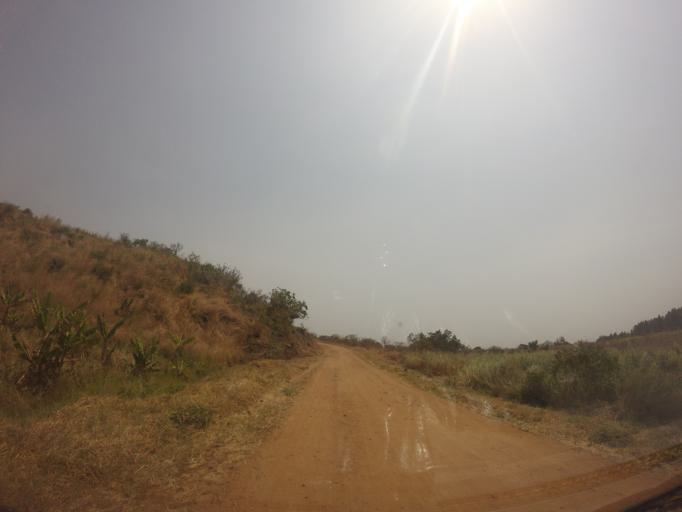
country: UG
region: Northern Region
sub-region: Arua District
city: Arua
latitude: 2.9240
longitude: 30.9920
